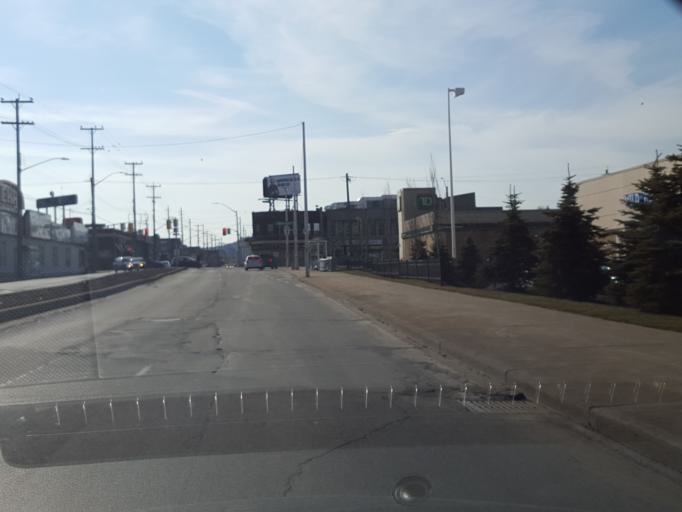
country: CA
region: Ontario
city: Hamilton
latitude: 43.2503
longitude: -79.8058
